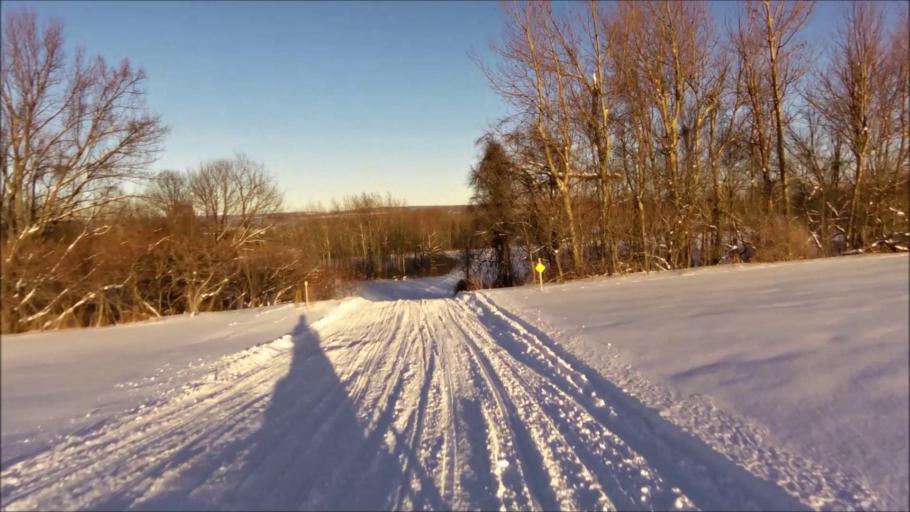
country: US
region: New York
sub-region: Chautauqua County
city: Celoron
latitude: 42.2266
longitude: -79.3181
